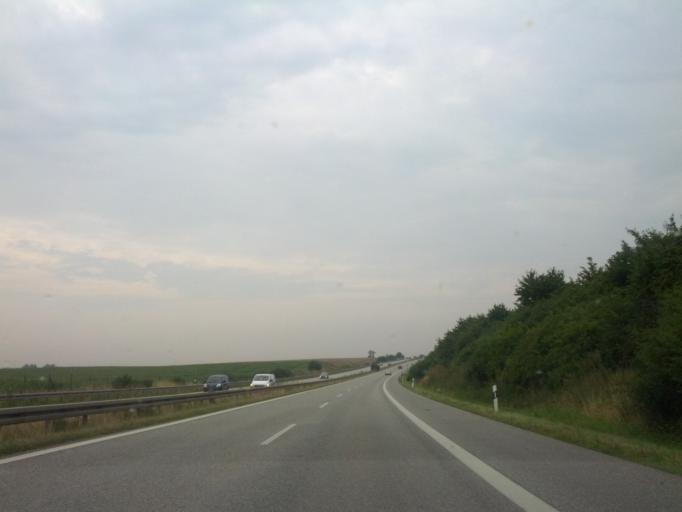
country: DE
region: Mecklenburg-Vorpommern
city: Kritzmow
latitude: 54.0613
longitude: 12.0448
